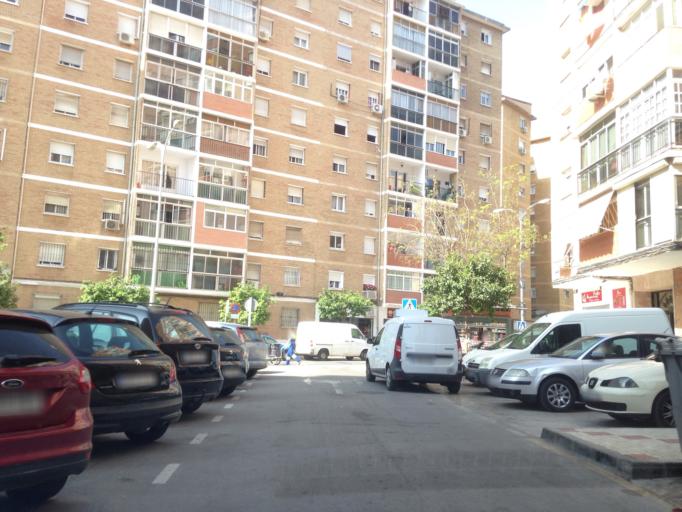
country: ES
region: Andalusia
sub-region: Provincia de Malaga
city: Malaga
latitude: 36.6984
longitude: -4.4541
